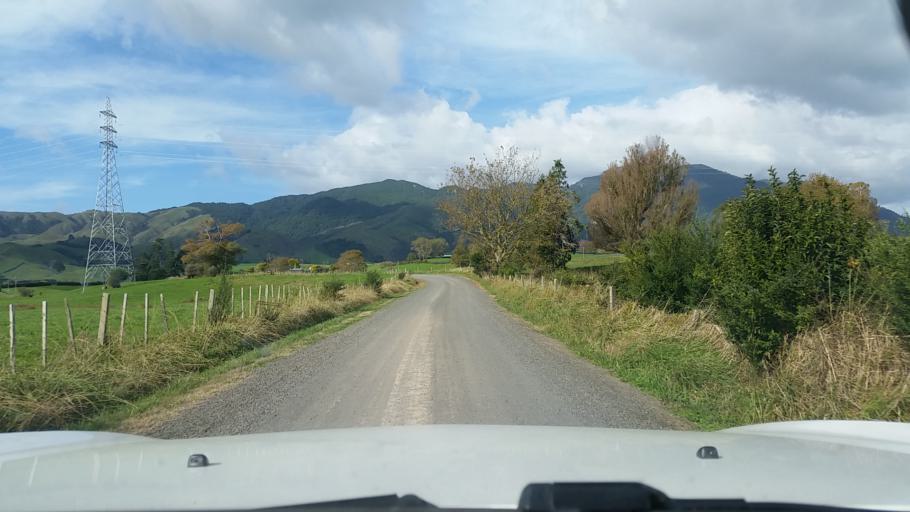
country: NZ
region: Waikato
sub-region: Hauraki District
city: Paeroa
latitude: -37.5008
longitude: 175.6910
